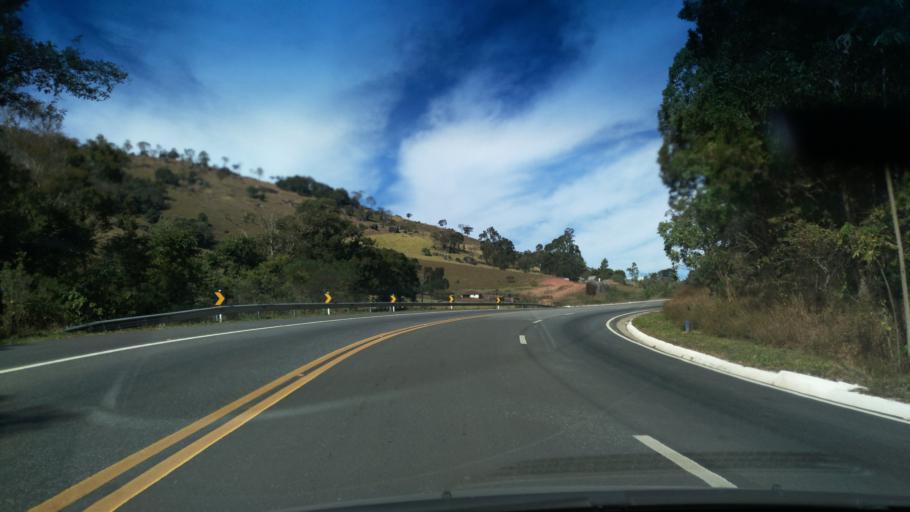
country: BR
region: Minas Gerais
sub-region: Borda Da Mata
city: Borda da Mata
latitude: -22.1207
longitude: -46.1801
